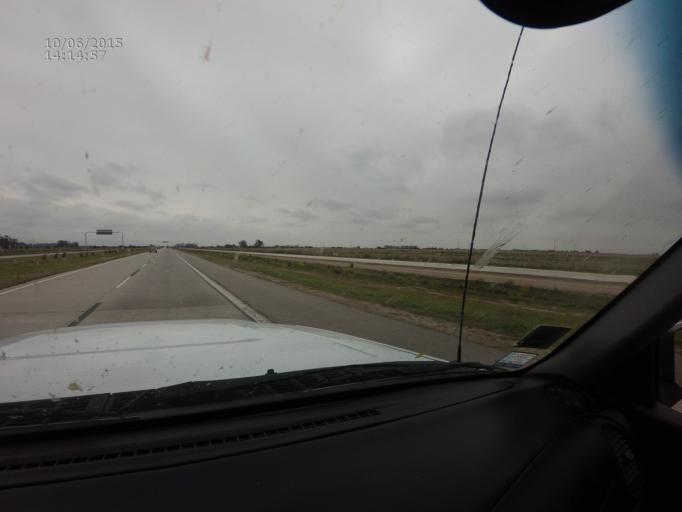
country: AR
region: Cordoba
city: Villa Maria
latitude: -32.4145
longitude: -63.1668
